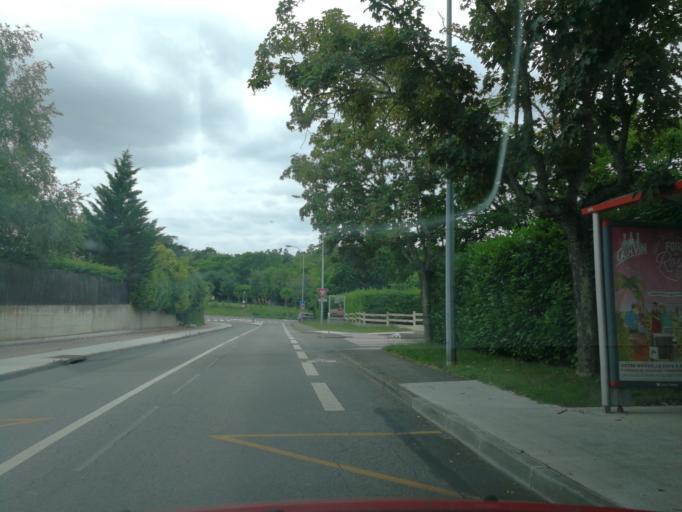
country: FR
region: Midi-Pyrenees
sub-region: Departement de la Haute-Garonne
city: Ramonville-Saint-Agne
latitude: 43.5355
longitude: 1.4732
